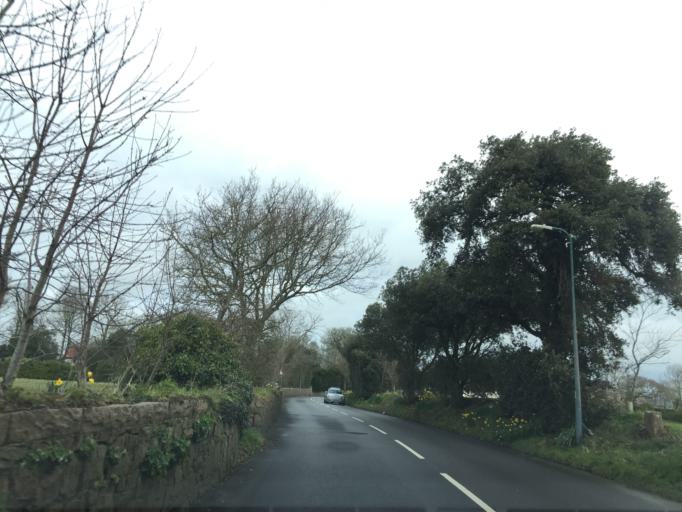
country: JE
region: St Helier
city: Saint Helier
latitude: 49.2113
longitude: -2.1417
